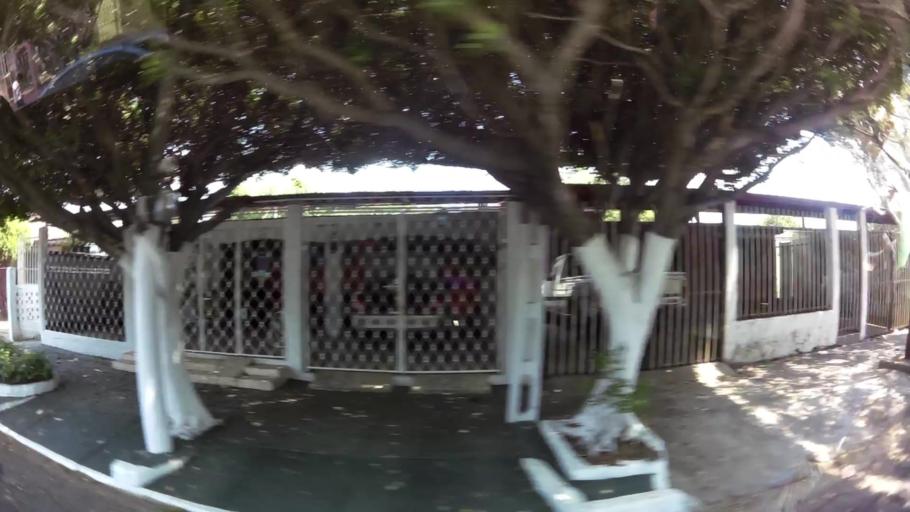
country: NI
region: Managua
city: Ciudad Sandino
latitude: 12.1531
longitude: -86.3130
